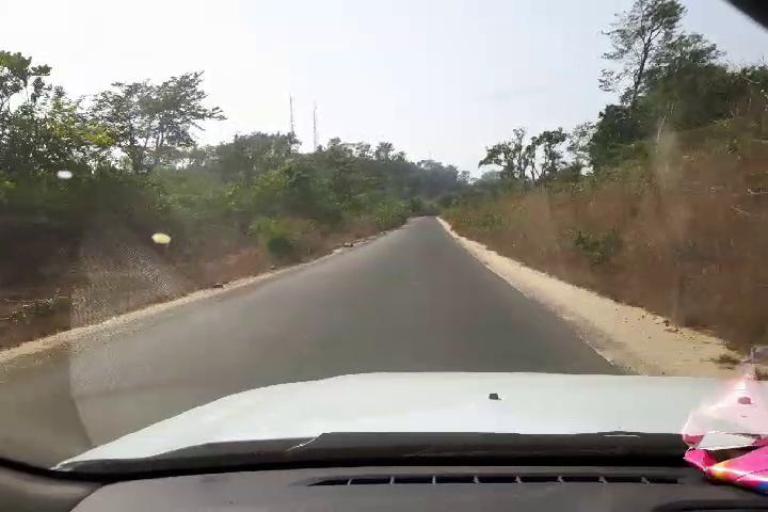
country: SL
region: Western Area
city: Waterloo
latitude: 8.2620
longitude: -13.1608
